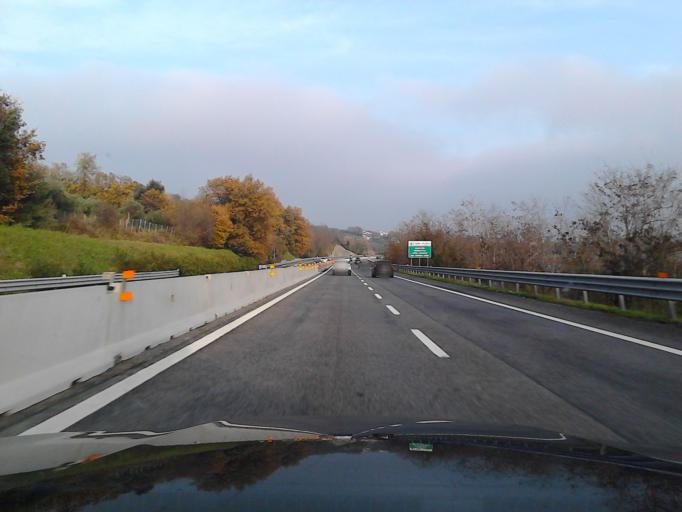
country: IT
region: Abruzzo
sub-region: Provincia di Chieti
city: Francavilla al Mare
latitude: 42.4163
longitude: 14.2425
